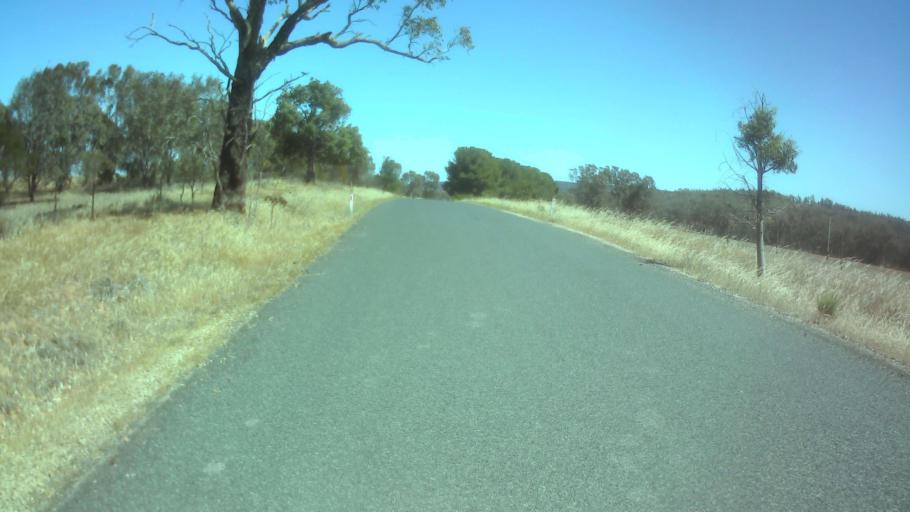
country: AU
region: New South Wales
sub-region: Weddin
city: Grenfell
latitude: -33.9422
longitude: 148.3871
